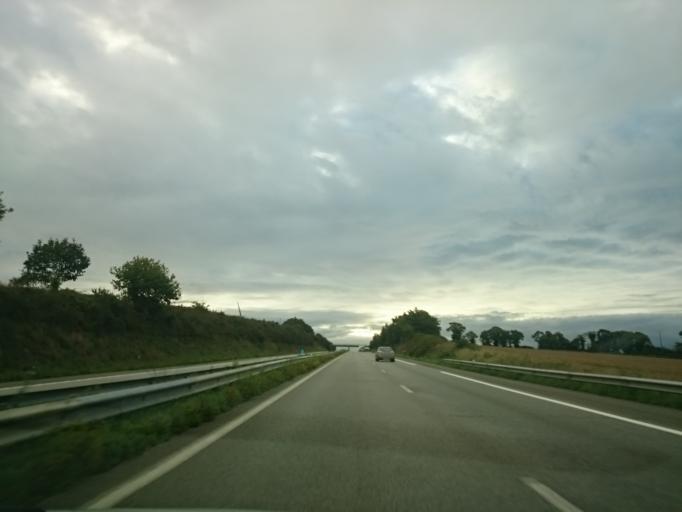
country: FR
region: Brittany
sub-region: Departement du Finistere
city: Chateaulin
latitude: 48.2211
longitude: -4.0651
